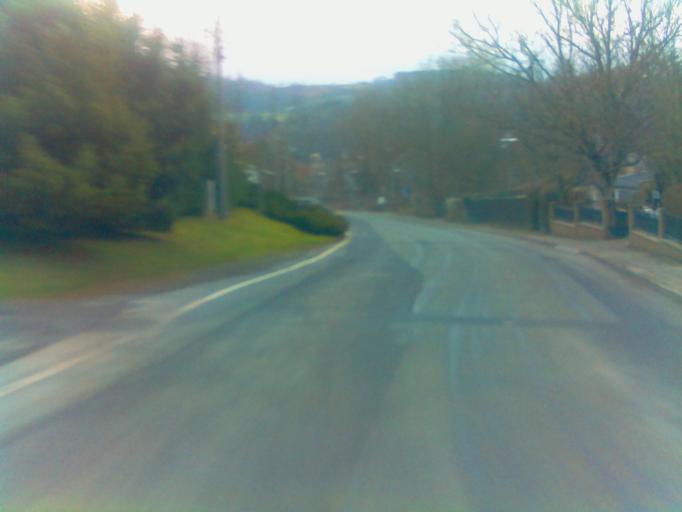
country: DE
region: Thuringia
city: Possneck
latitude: 50.6956
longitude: 11.5717
